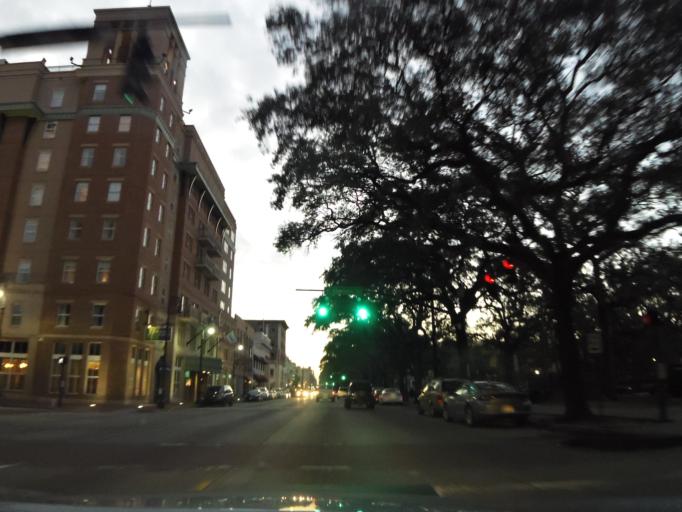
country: US
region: Georgia
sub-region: Chatham County
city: Savannah
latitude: 32.0803
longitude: -81.0887
